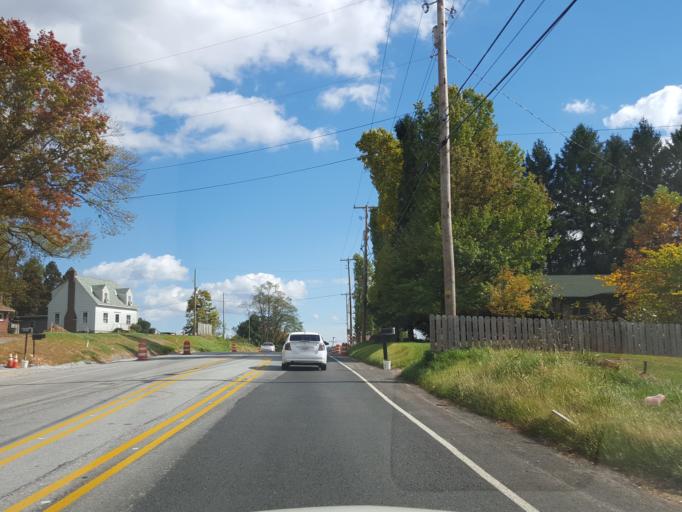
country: US
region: Pennsylvania
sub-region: York County
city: Stonybrook
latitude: 39.9545
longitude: -76.6514
